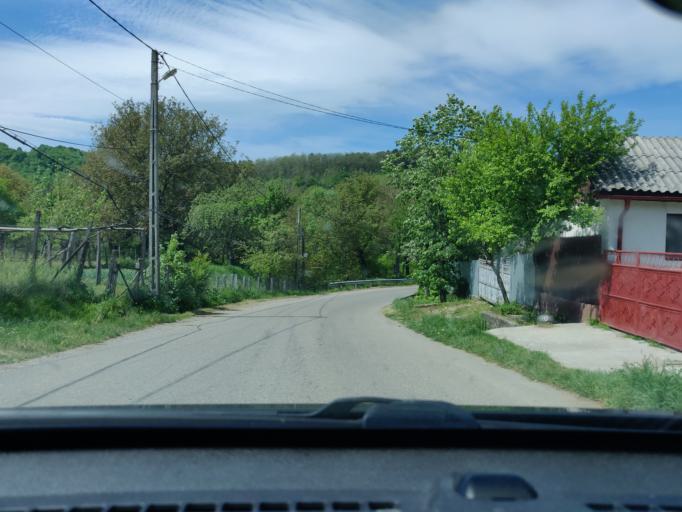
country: RO
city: Vizantea-Manastireasca
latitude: 45.9748
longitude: 26.8117
